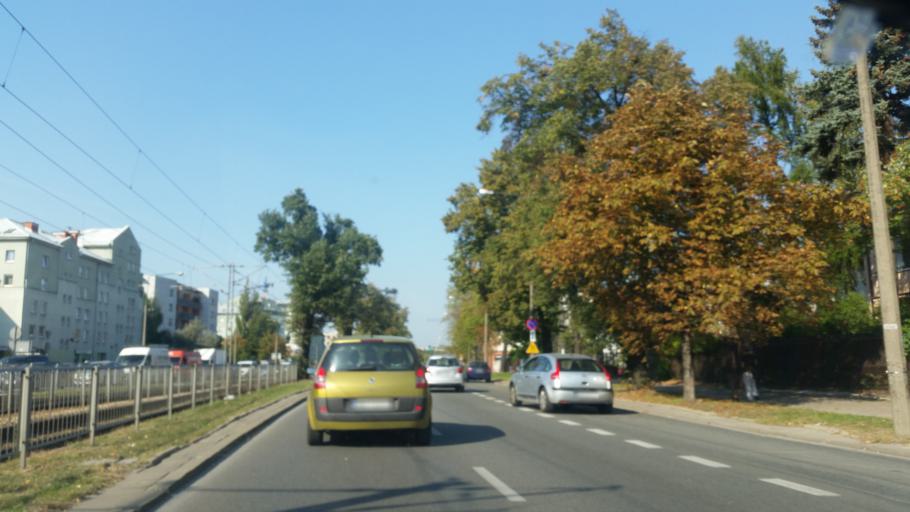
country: PL
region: Masovian Voivodeship
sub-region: Warszawa
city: Bemowo
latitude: 52.2298
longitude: 20.9153
